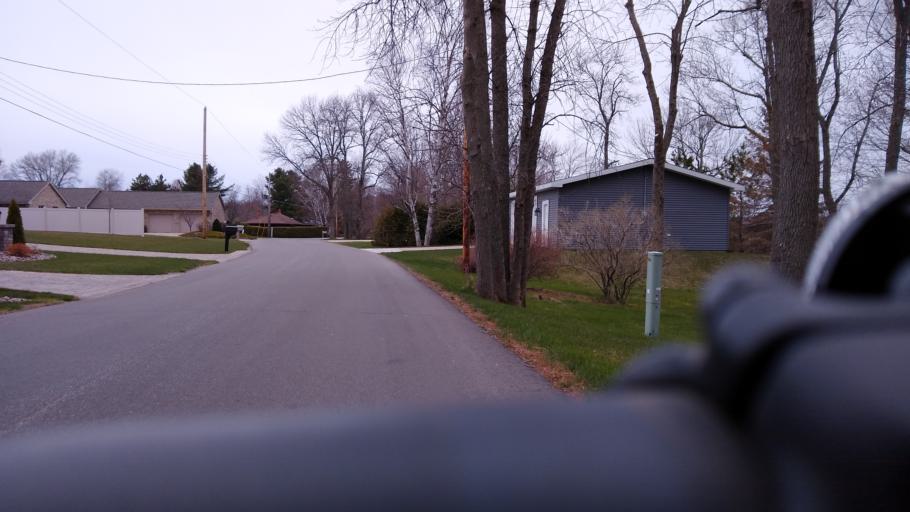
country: US
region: Michigan
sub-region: Delta County
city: Escanaba
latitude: 45.7029
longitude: -87.0912
